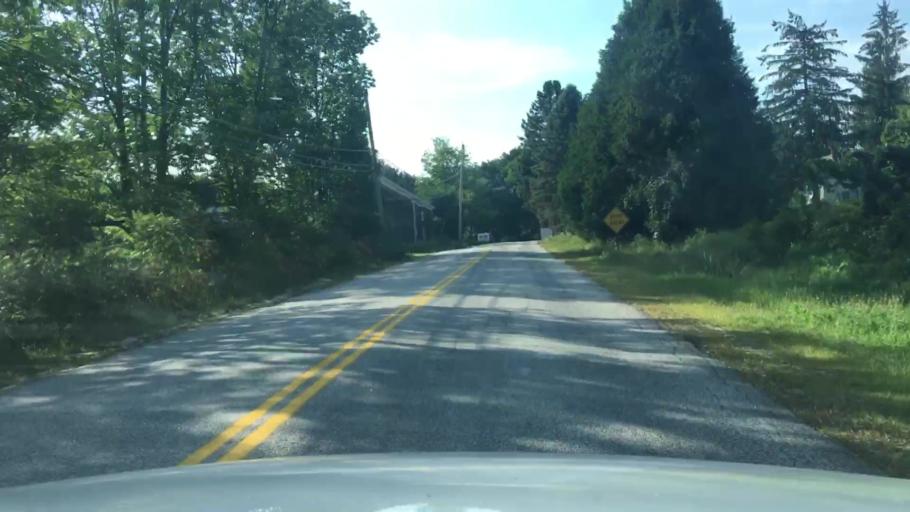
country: US
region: Maine
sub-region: Cumberland County
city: New Gloucester
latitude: 43.9417
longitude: -70.2986
